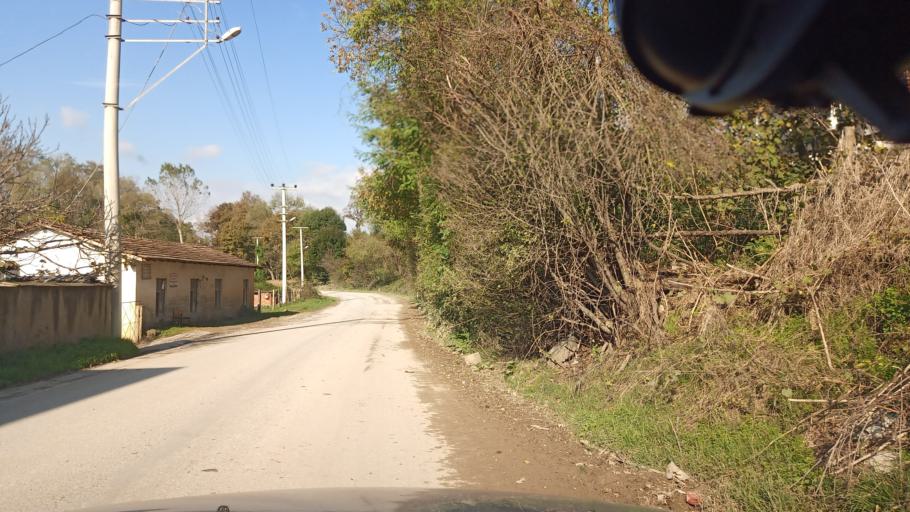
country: TR
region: Sakarya
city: Kaynarca
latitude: 41.0935
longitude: 30.4425
